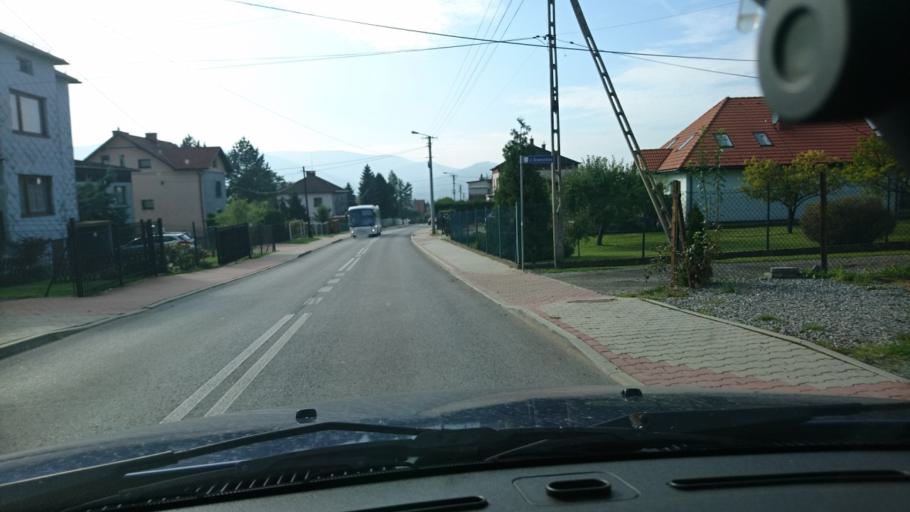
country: PL
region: Silesian Voivodeship
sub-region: Powiat bielski
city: Wilkowice
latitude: 49.7590
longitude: 19.1114
